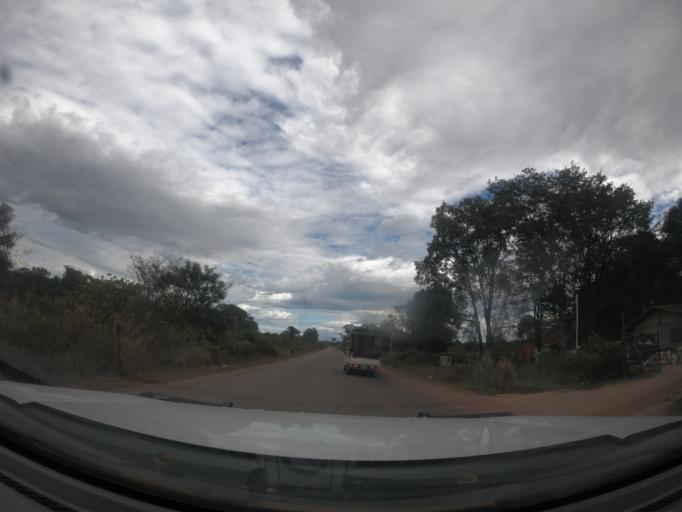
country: LA
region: Bolikhamxai
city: Muang Pakxan
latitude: 18.3772
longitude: 103.7363
